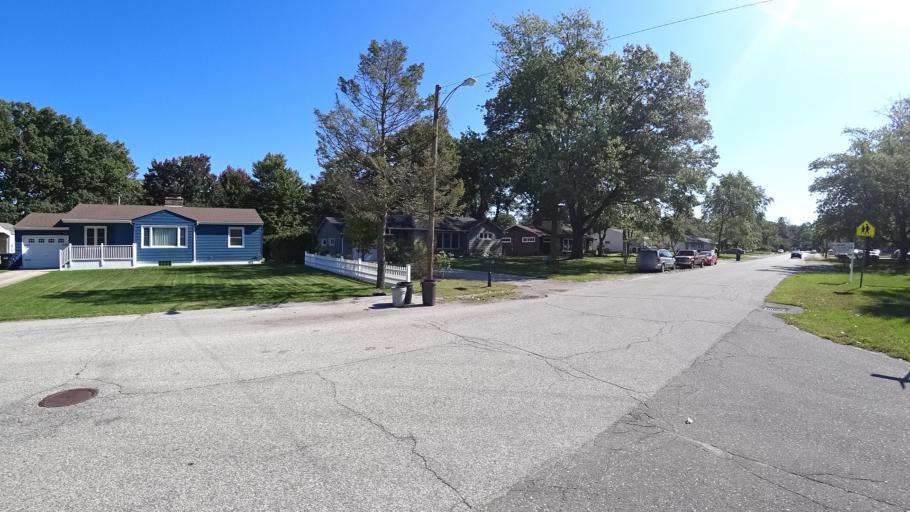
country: US
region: Indiana
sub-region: LaPorte County
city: Michigan City
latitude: 41.6935
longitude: -86.8855
